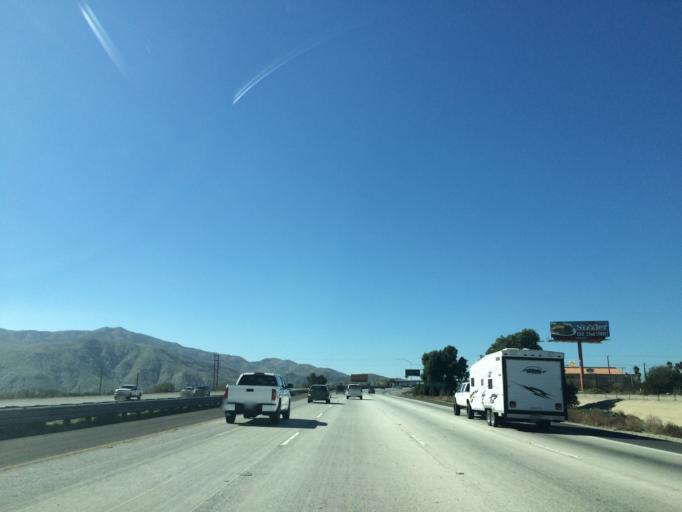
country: US
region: California
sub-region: Riverside County
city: Cabazon
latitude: 33.9193
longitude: -116.7693
